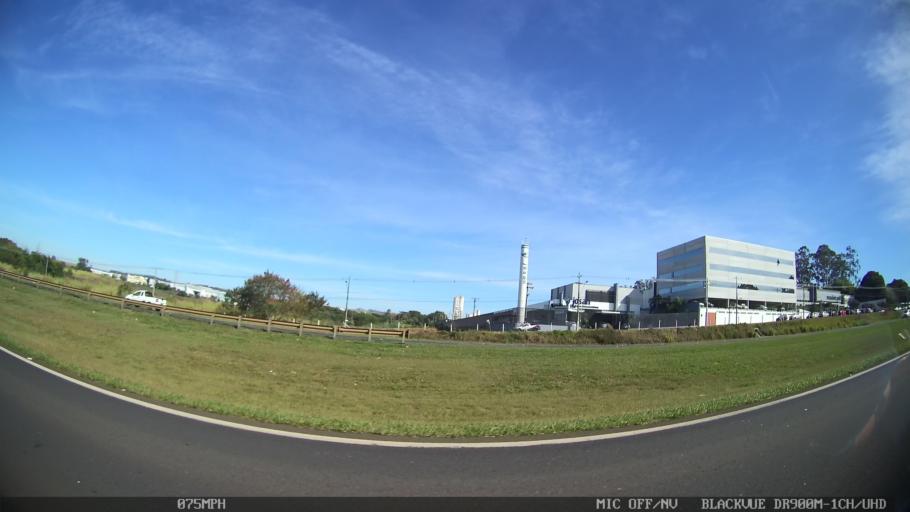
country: BR
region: Sao Paulo
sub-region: Leme
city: Leme
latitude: -22.2075
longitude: -47.3945
